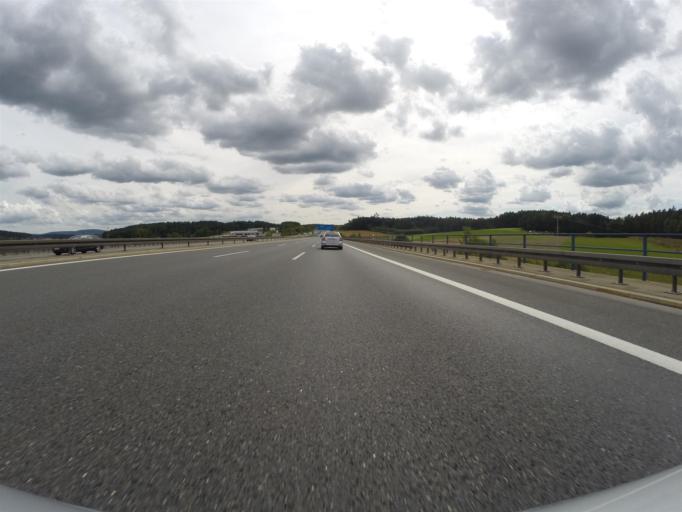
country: DE
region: Bavaria
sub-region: Regierungsbezirk Mittelfranken
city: Schnaittach
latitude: 49.5735
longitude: 11.3378
